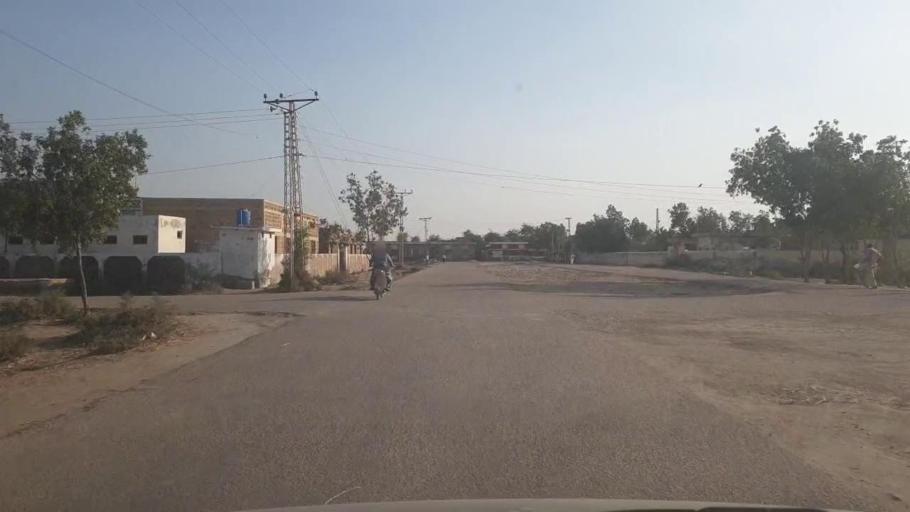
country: PK
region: Sindh
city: Badin
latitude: 24.6528
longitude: 68.8276
